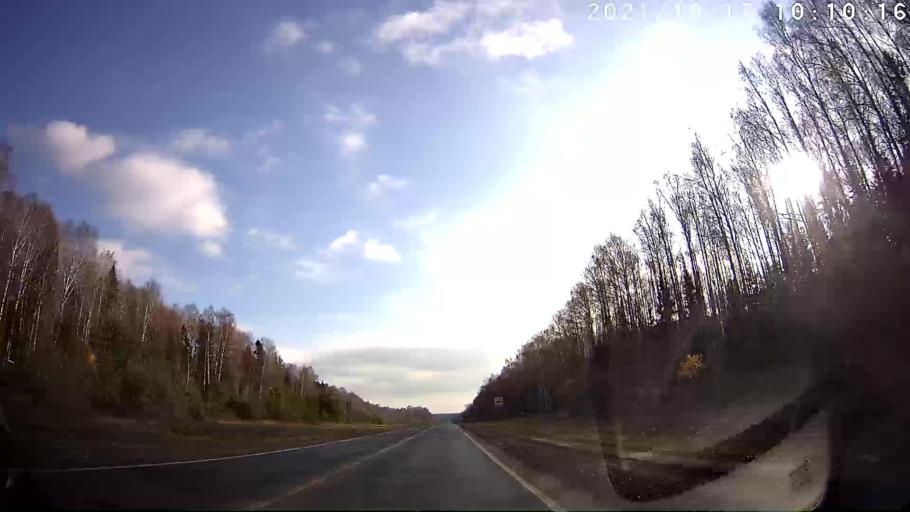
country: RU
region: Mariy-El
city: Sovetskiy
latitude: 56.7443
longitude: 48.3631
